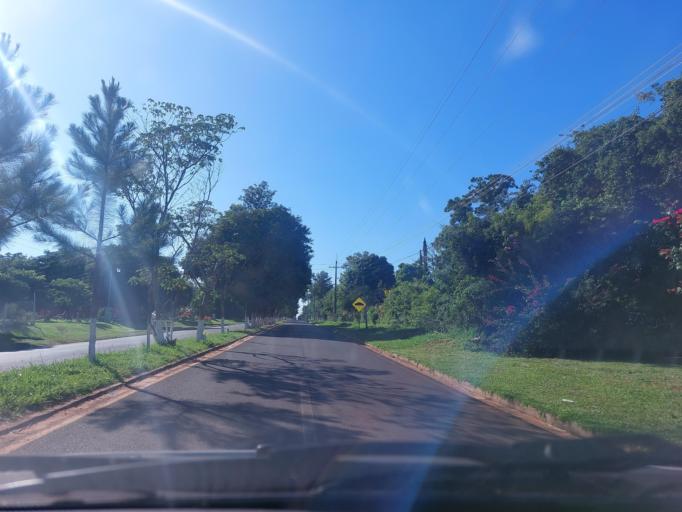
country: PY
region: San Pedro
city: Guayaybi
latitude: -24.5316
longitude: -56.4523
